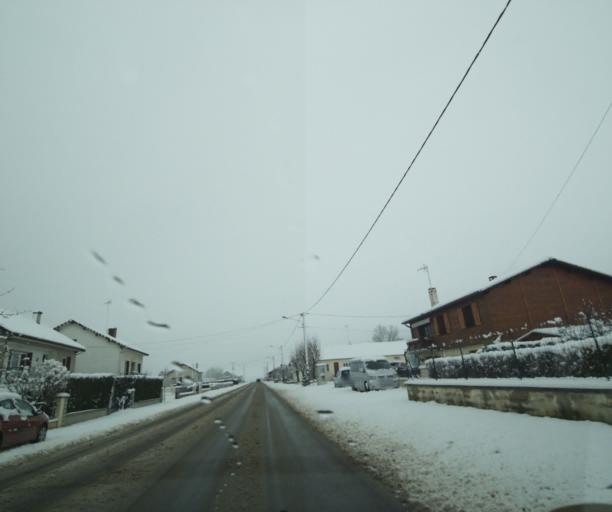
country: FR
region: Champagne-Ardenne
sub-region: Departement de la Haute-Marne
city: Wassy
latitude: 48.5277
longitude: 4.9283
